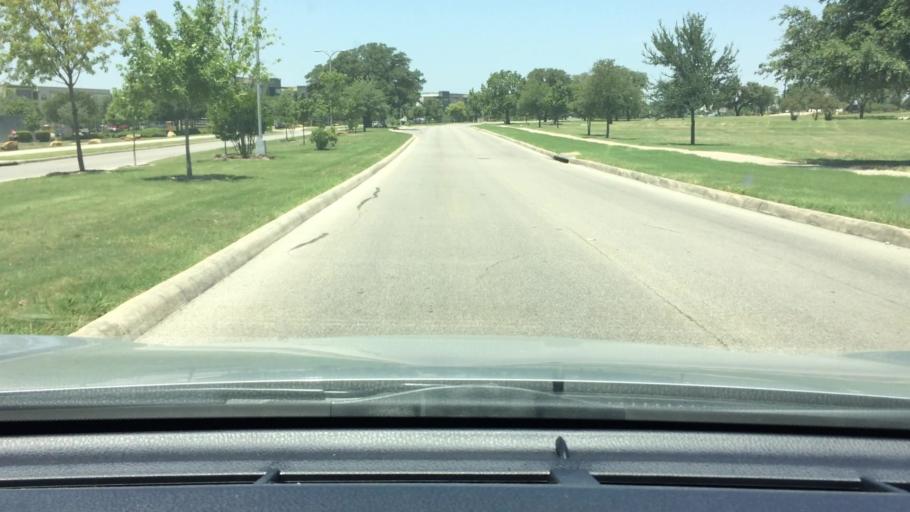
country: US
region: Texas
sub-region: Bexar County
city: San Antonio
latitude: 29.3475
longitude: -98.4462
